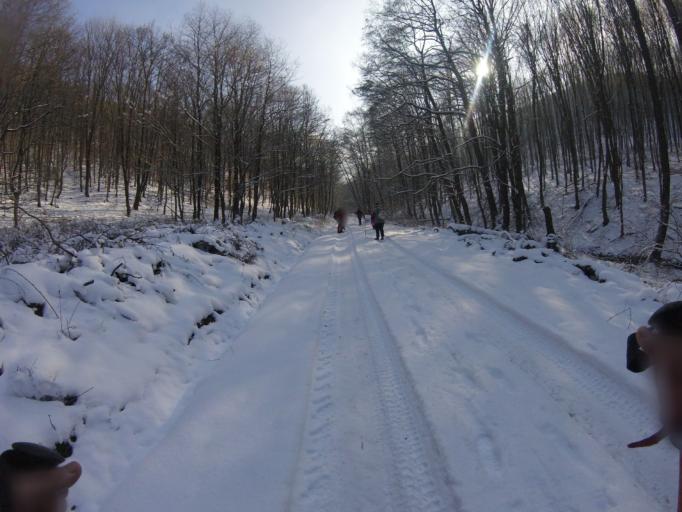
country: HU
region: Heves
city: Belapatfalva
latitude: 48.0605
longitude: 20.3810
